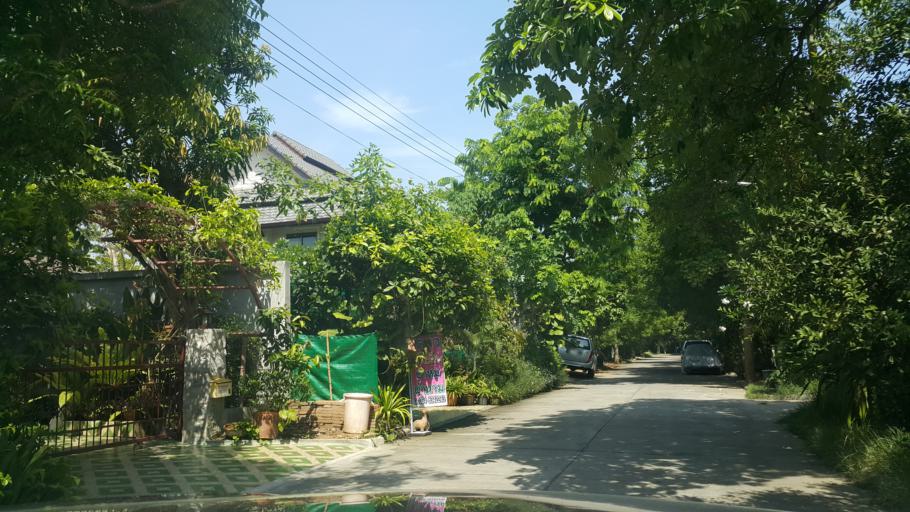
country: TH
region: Chiang Mai
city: Hang Dong
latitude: 18.7265
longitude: 98.9684
